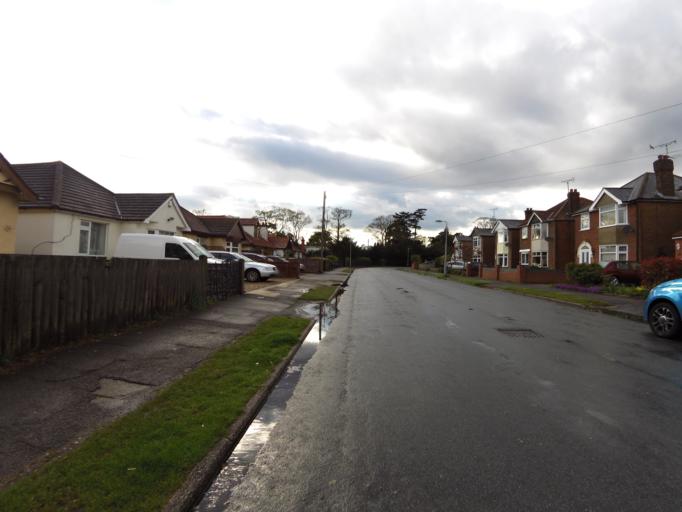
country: GB
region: England
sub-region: Suffolk
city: Kesgrave
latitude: 52.0501
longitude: 1.1969
